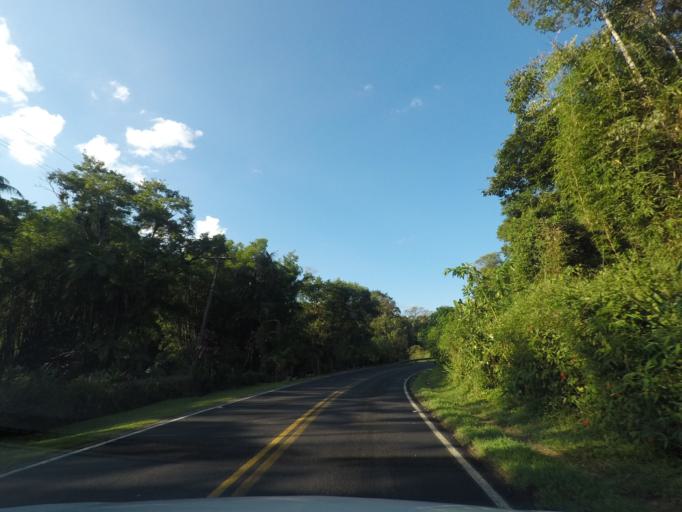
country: BR
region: Parana
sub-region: Antonina
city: Antonina
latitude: -25.3971
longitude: -48.8695
